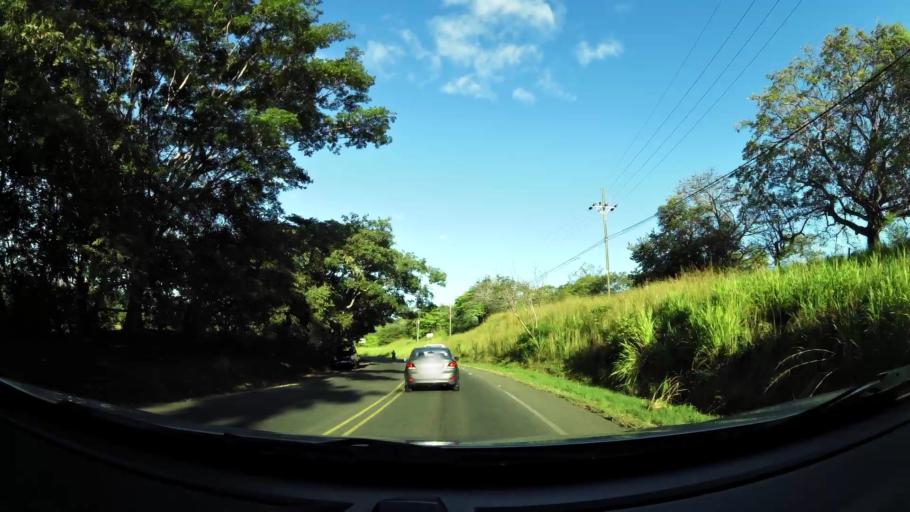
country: CR
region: Puntarenas
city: Miramar
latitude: 10.1011
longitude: -84.8062
